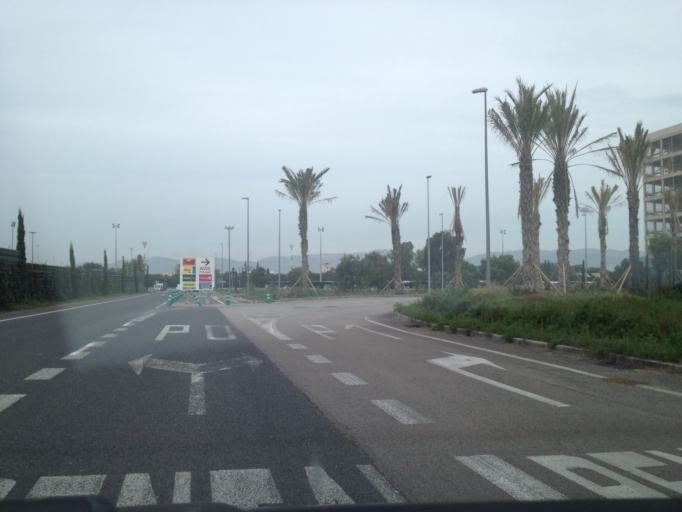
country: ES
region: Balearic Islands
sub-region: Illes Balears
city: s'Arenal
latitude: 39.5451
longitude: 2.7268
